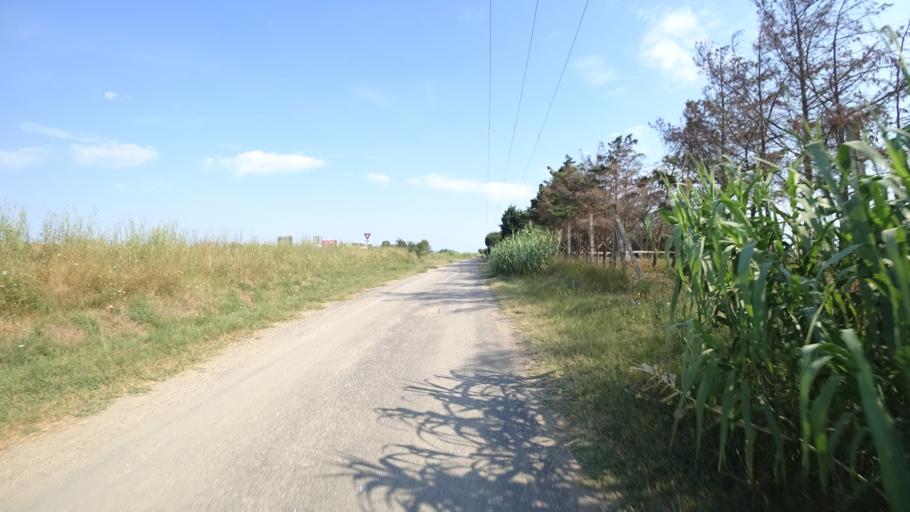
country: FR
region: Languedoc-Roussillon
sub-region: Departement des Pyrenees-Orientales
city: Le Barcares
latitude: 42.7763
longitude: 3.0165
